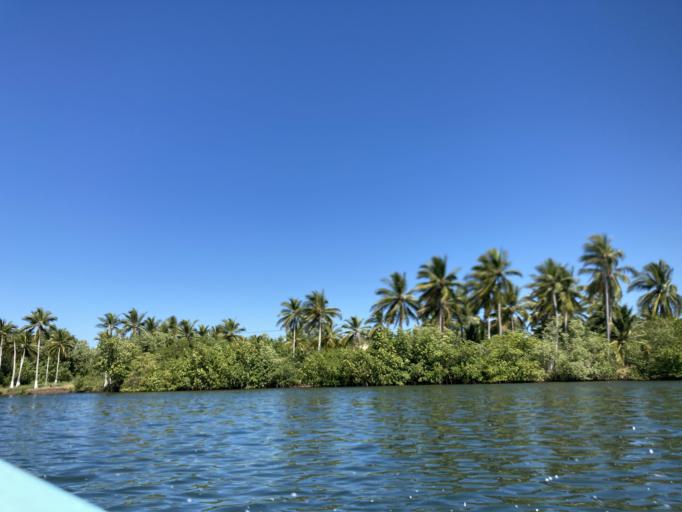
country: GT
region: Jutiapa
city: Pasaco
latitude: 13.8091
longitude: -90.2715
